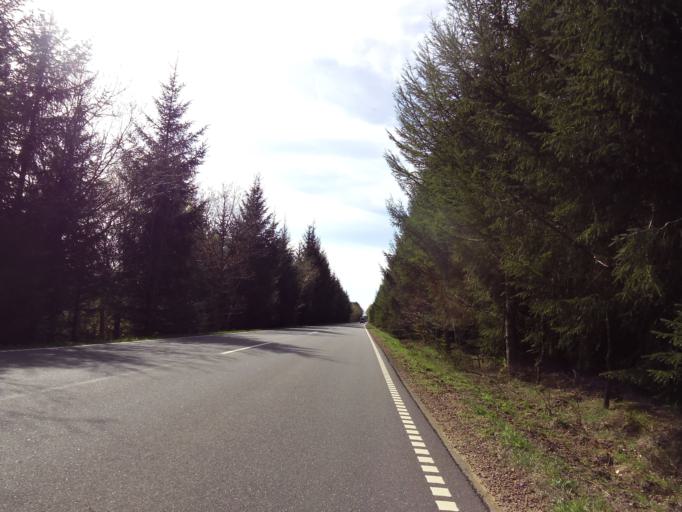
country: DK
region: Central Jutland
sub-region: Holstebro Kommune
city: Vinderup
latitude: 56.4682
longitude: 8.9178
